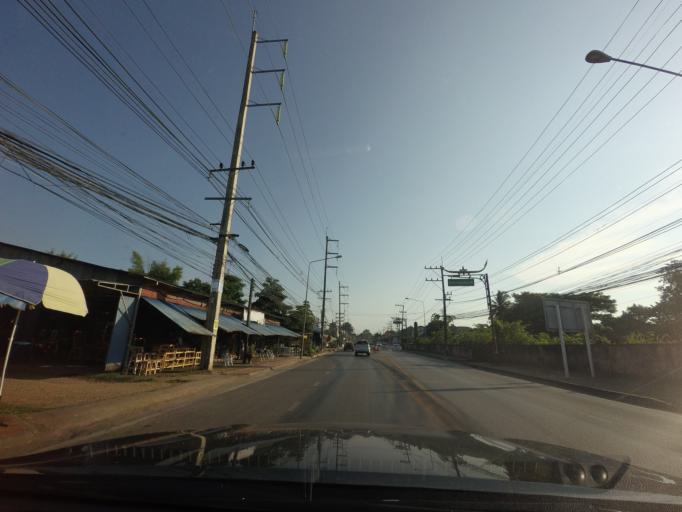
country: TH
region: Nan
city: Nan
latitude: 18.7719
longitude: 100.7651
